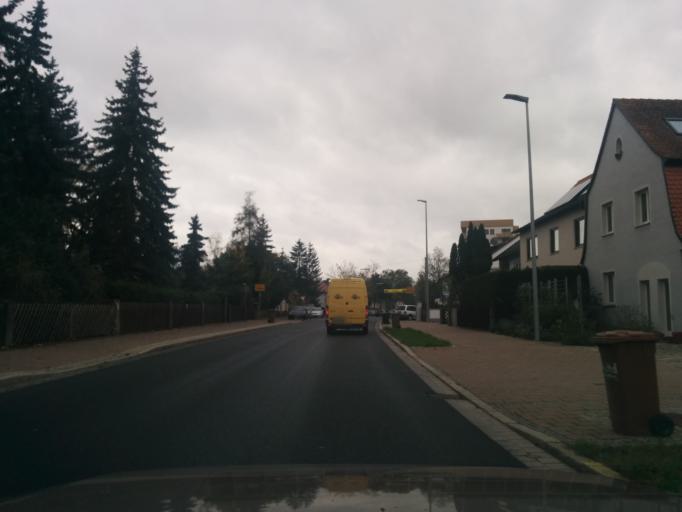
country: DE
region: Bavaria
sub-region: Regierungsbezirk Mittelfranken
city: Buckenhof
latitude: 49.5936
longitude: 11.0457
